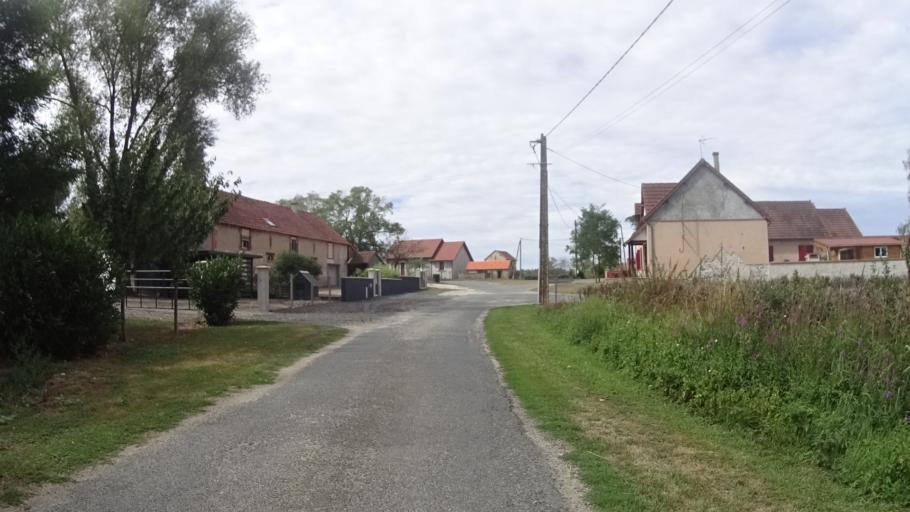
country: FR
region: Auvergne
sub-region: Departement de l'Allier
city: Beaulon
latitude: 46.6458
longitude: 3.6683
